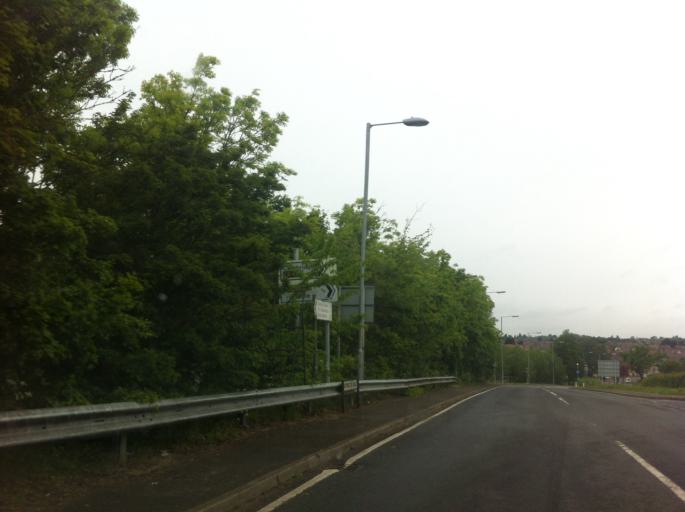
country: GB
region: England
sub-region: Northamptonshire
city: Wellingborough
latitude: 52.2852
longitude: -0.6974
